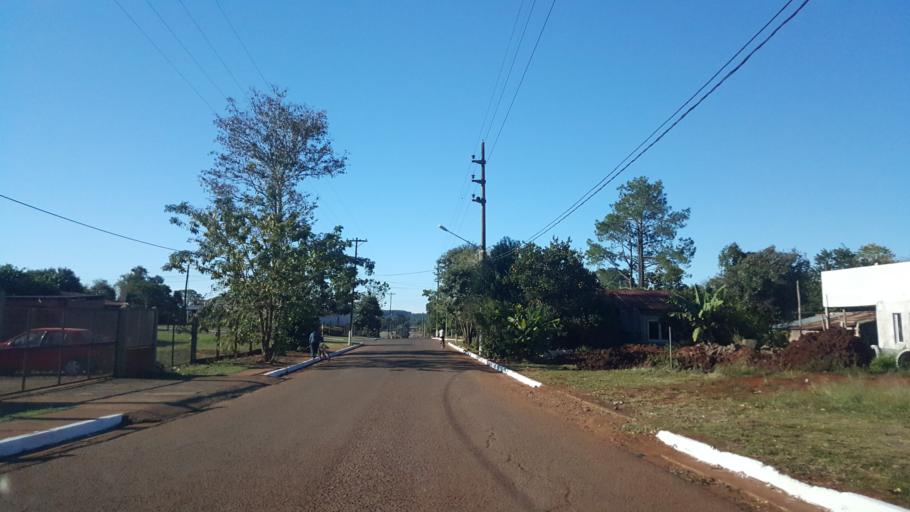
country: AR
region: Misiones
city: Gobernador Roca
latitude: -27.1872
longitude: -55.4640
